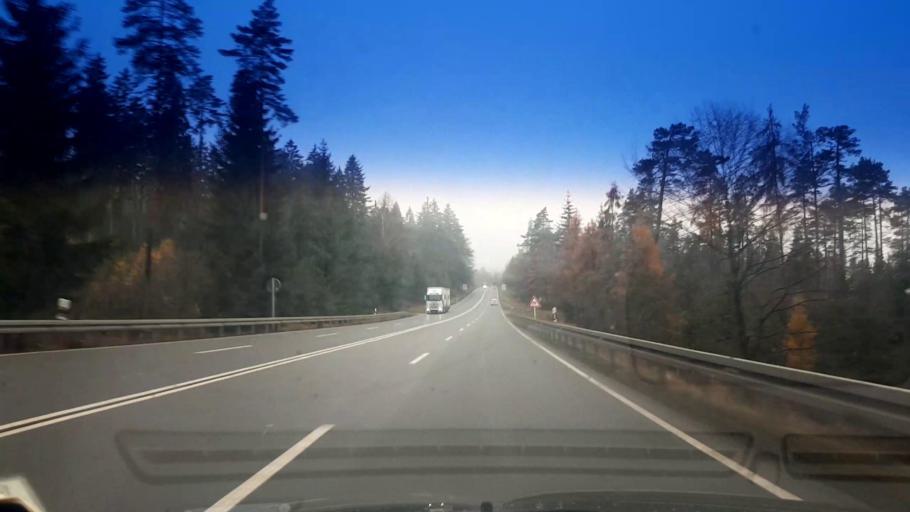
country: DE
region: Bavaria
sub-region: Upper Franconia
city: Nagel
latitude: 50.0022
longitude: 11.9147
